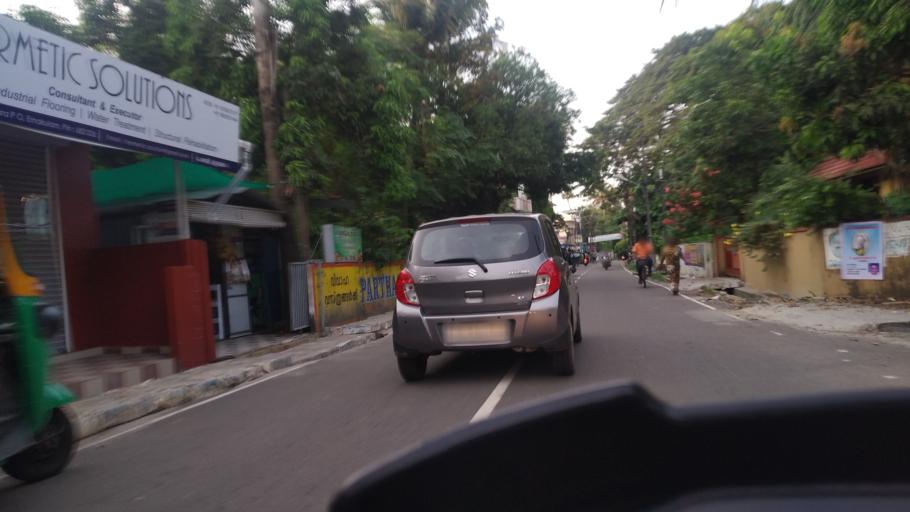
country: IN
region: Kerala
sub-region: Ernakulam
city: Elur
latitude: 10.0171
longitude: 76.2846
